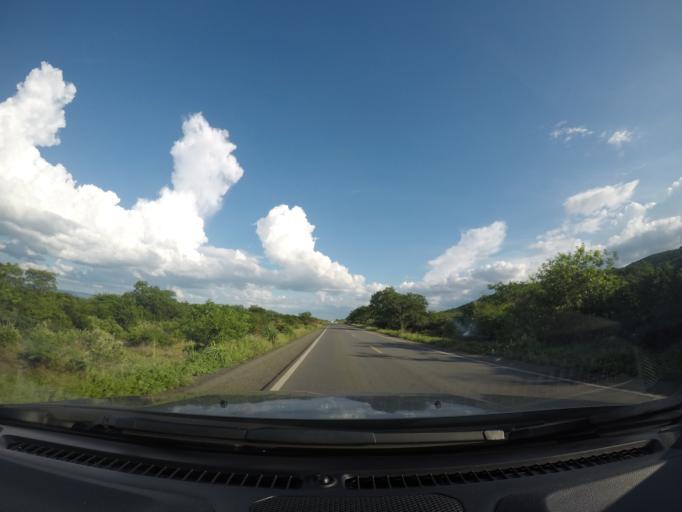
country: BR
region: Bahia
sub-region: Oliveira Dos Brejinhos
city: Oliveira dos Brejinhos
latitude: -12.0739
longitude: -42.9506
